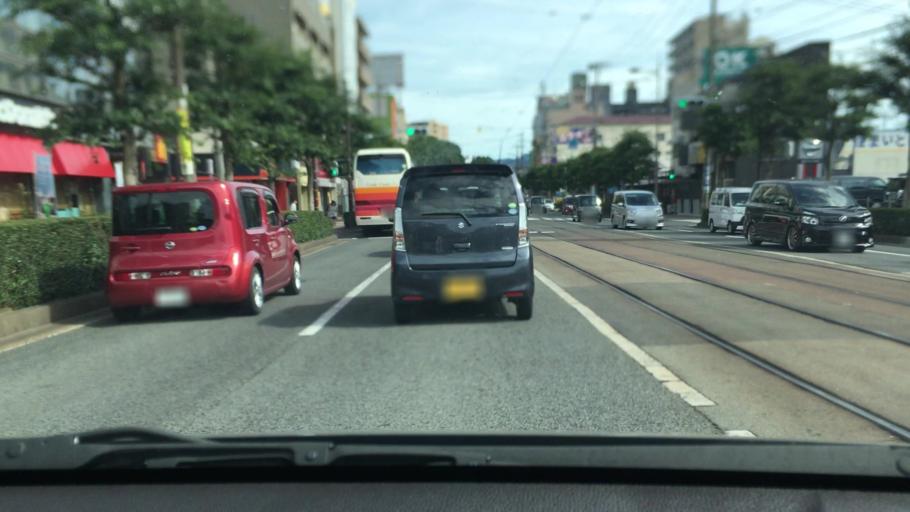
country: JP
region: Nagasaki
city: Obita
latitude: 32.7874
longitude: 129.8618
